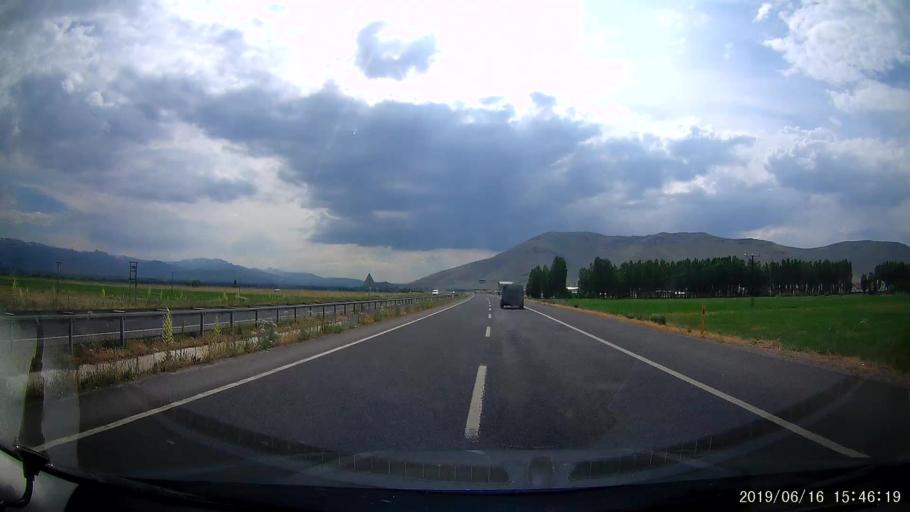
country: TR
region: Erzurum
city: Pasinler
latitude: 39.9902
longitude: 41.7469
